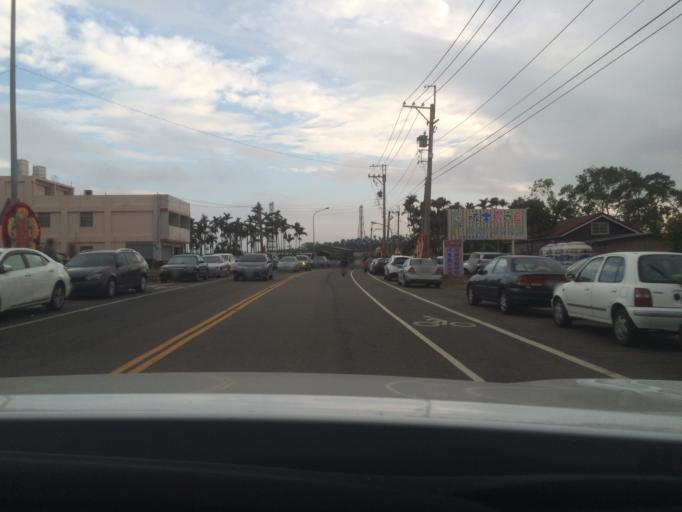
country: TW
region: Taiwan
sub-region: Nantou
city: Nantou
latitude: 23.9308
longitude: 120.6388
